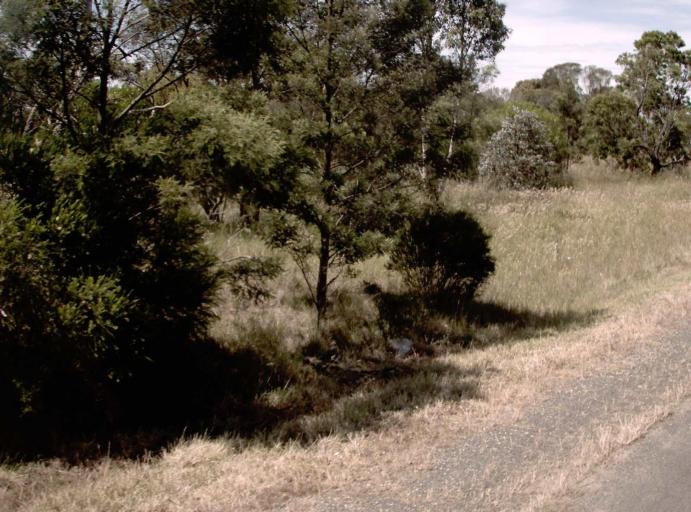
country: AU
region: Victoria
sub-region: Wellington
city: Sale
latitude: -38.1039
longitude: 146.9262
